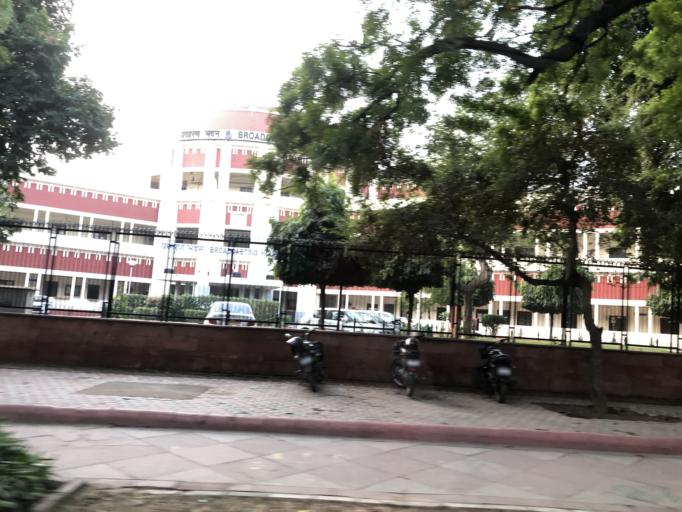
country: IN
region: NCT
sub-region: New Delhi
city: New Delhi
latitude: 28.6214
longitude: 77.2113
